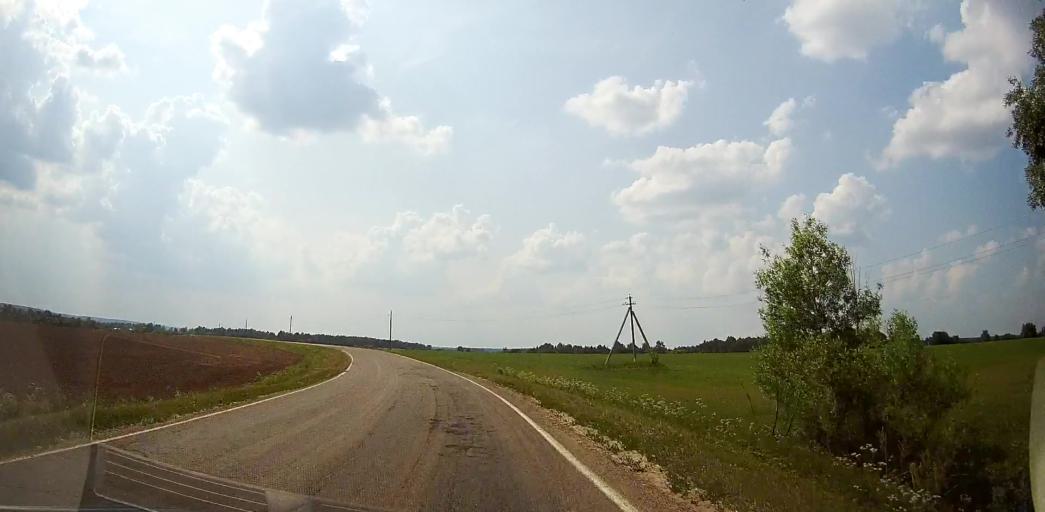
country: RU
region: Moskovskaya
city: Malino
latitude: 55.0611
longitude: 38.0984
